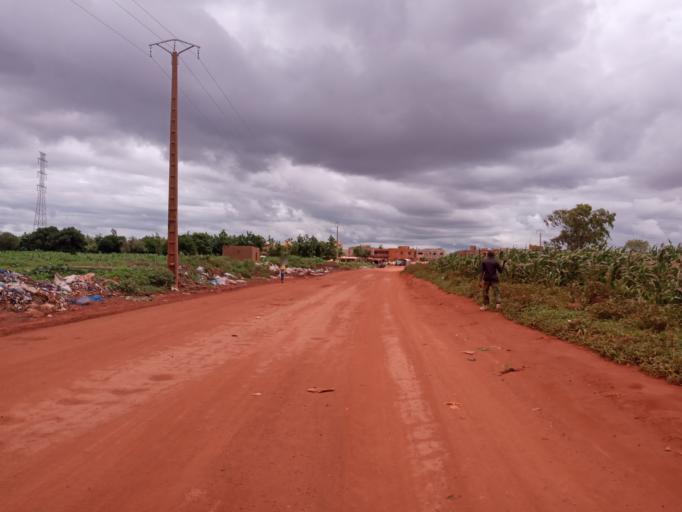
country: ML
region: Bamako
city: Bamako
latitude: 12.5466
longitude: -7.9949
